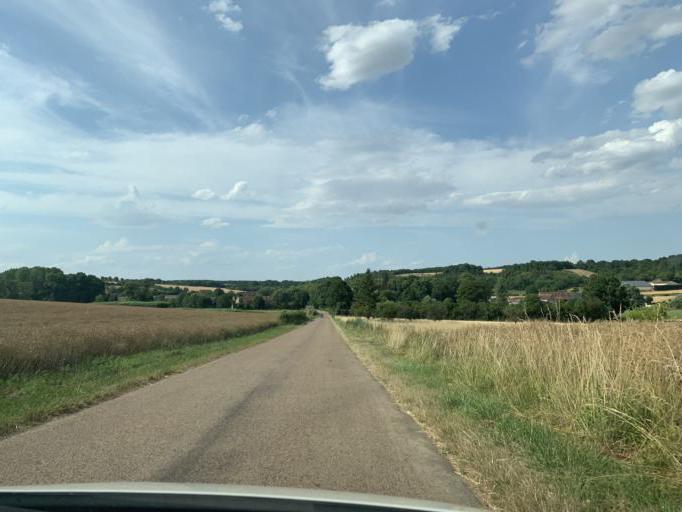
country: FR
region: Bourgogne
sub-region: Departement de l'Yonne
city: Fontenailles
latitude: 47.4763
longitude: 3.4221
